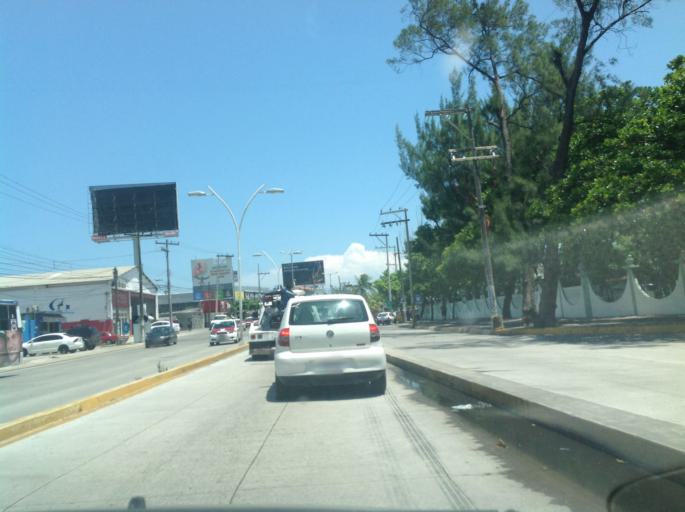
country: MX
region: Veracruz
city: Veracruz
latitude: 19.1454
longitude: -96.1270
